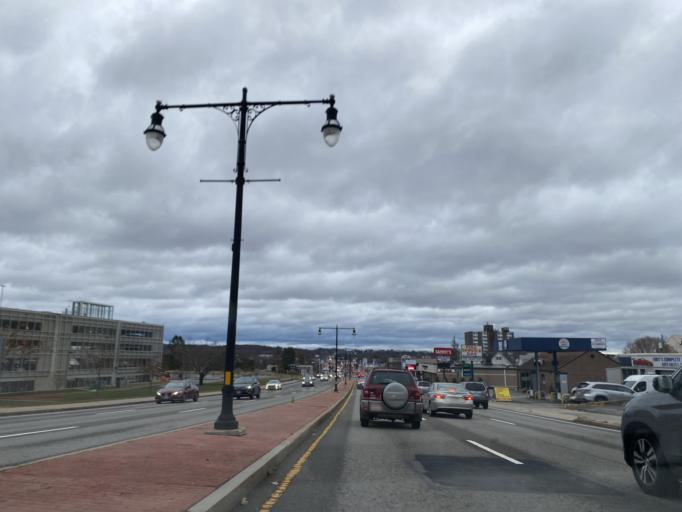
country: US
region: Massachusetts
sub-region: Worcester County
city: Hamilton
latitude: 42.2739
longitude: -71.7632
